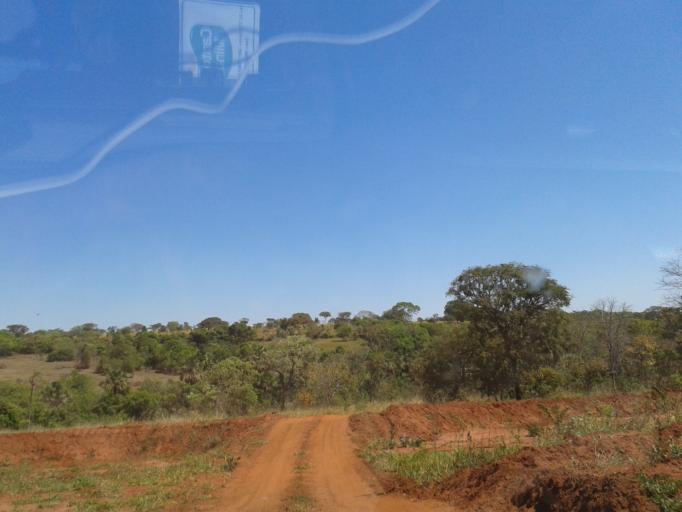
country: BR
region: Minas Gerais
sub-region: Ituiutaba
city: Ituiutaba
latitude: -19.0902
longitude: -49.2588
